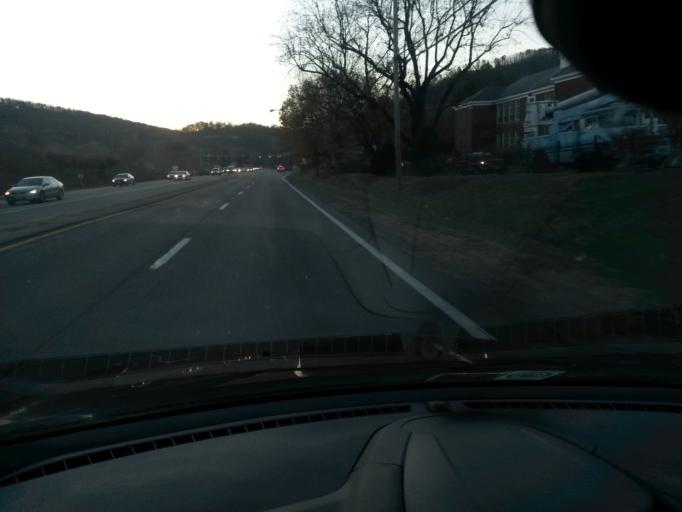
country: US
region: Virginia
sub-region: Roanoke County
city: Narrows
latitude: 37.2043
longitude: -79.9516
